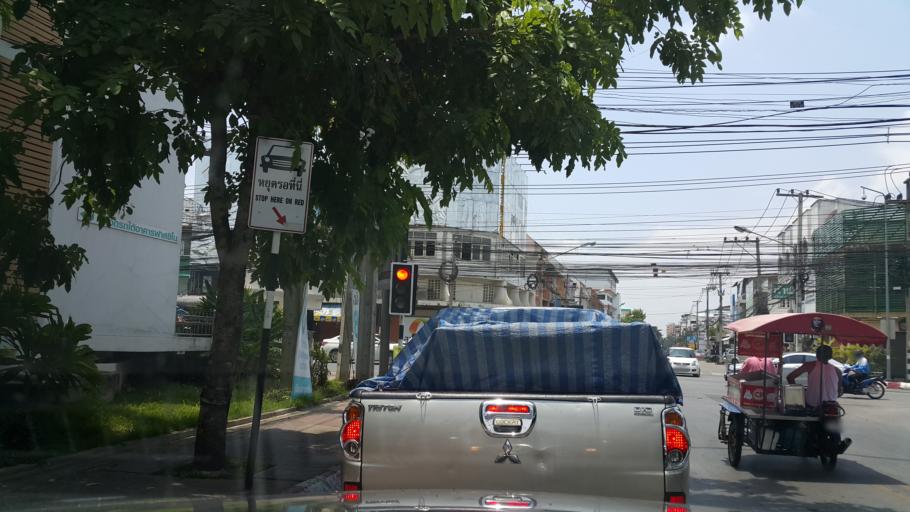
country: TH
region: Chiang Mai
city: Chiang Mai
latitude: 18.8008
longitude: 99.0135
